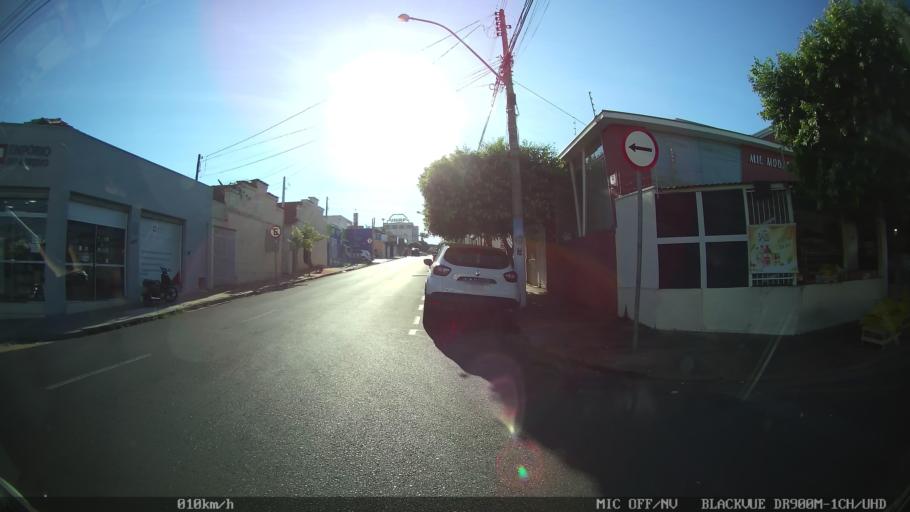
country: BR
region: Sao Paulo
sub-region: Sao Jose Do Rio Preto
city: Sao Jose do Rio Preto
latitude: -20.8101
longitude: -49.3888
